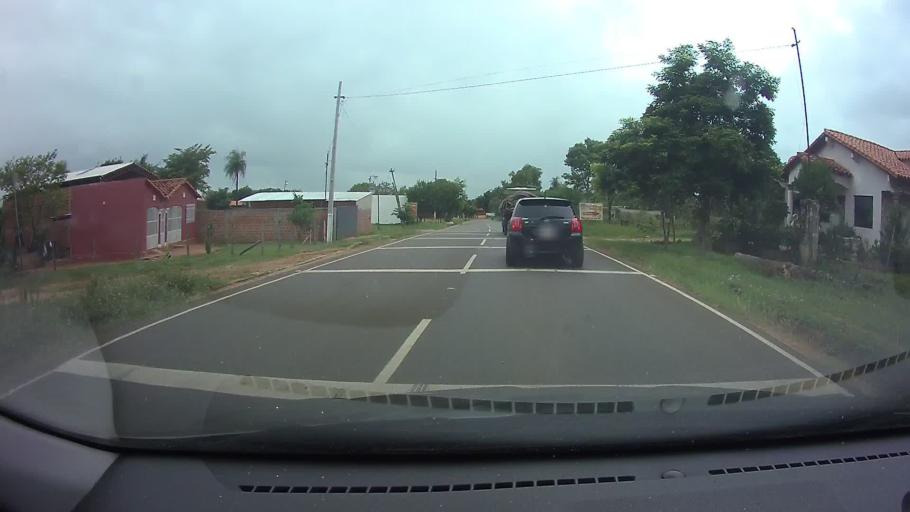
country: PY
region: Paraguari
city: Carapegua
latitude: -25.7600
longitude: -57.2530
